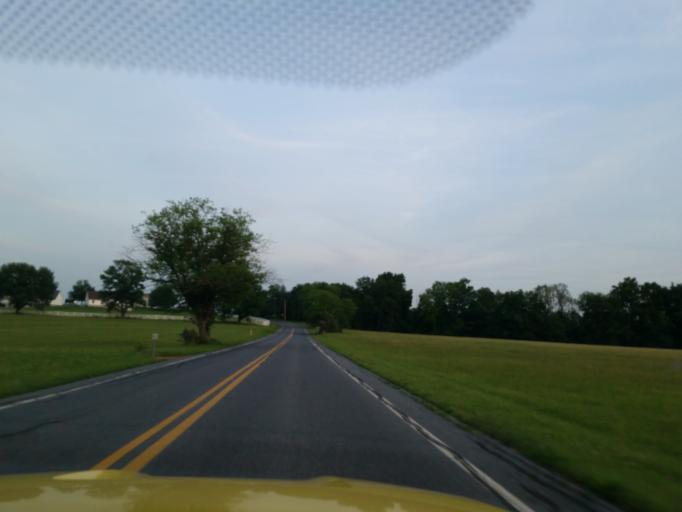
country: US
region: Pennsylvania
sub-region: Lebanon County
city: Palmyra
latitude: 40.4155
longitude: -76.6065
